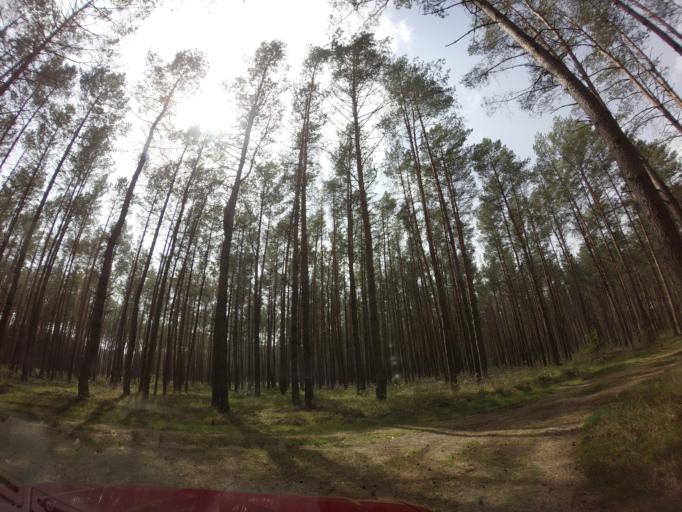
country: PL
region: West Pomeranian Voivodeship
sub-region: Powiat choszczenski
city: Drawno
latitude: 53.2689
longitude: 15.7133
